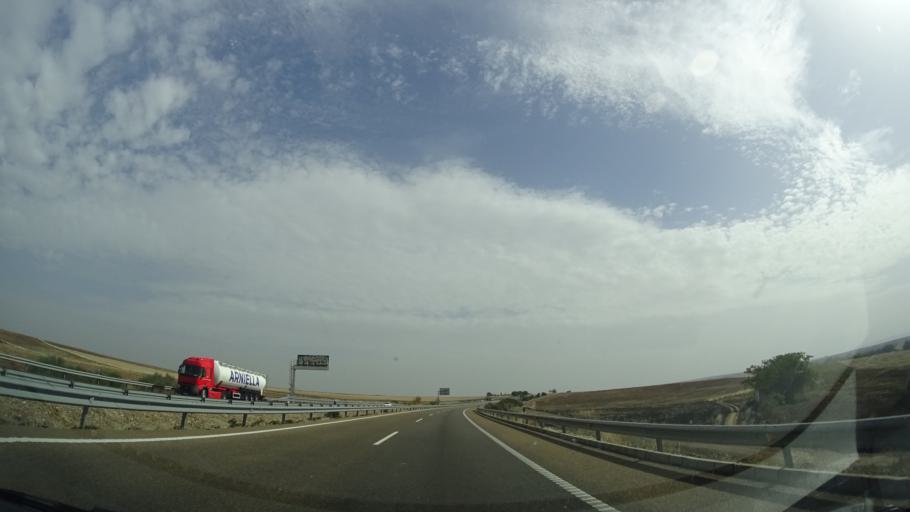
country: ES
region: Extremadura
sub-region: Provincia de Badajoz
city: Merida
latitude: 38.9463
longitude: -6.3220
